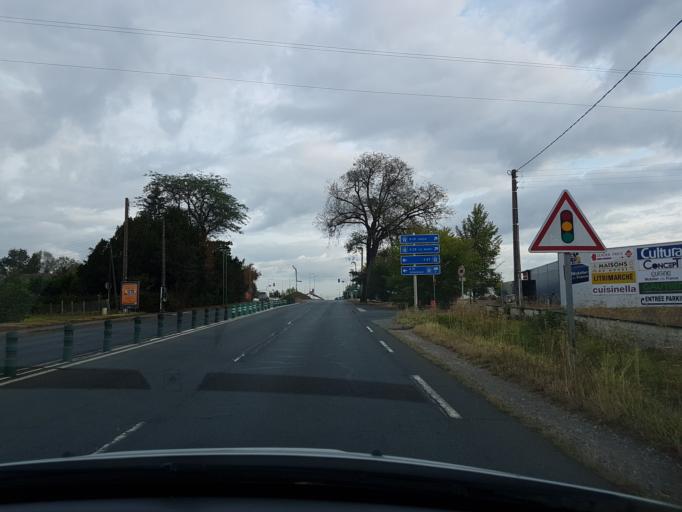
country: FR
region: Centre
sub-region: Departement d'Indre-et-Loire
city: Chambray-les-Tours
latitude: 47.3426
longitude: 0.7030
